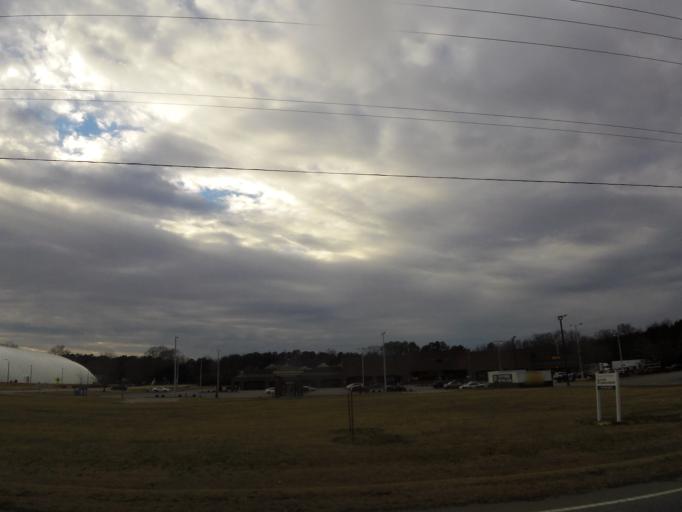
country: US
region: North Carolina
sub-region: Nash County
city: Rocky Mount
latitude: 36.0228
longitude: -77.7692
